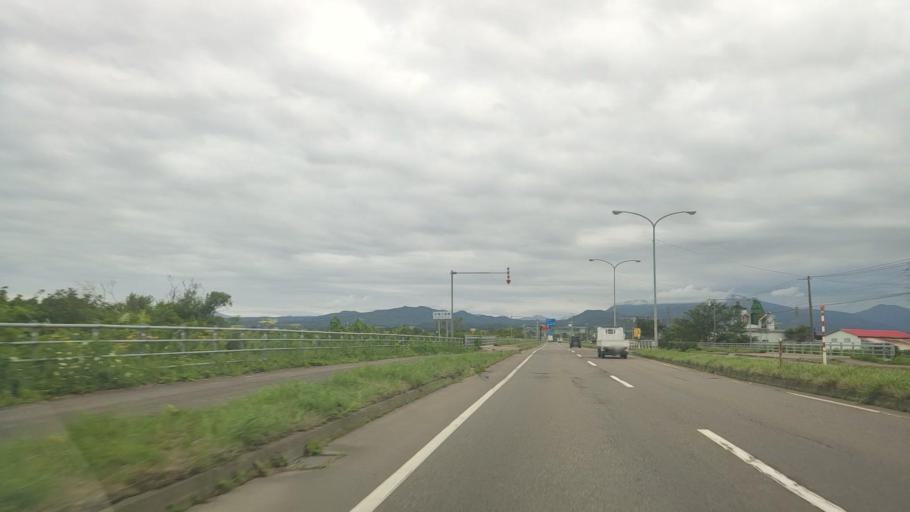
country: JP
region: Hokkaido
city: Nanae
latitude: 42.2717
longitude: 140.2725
